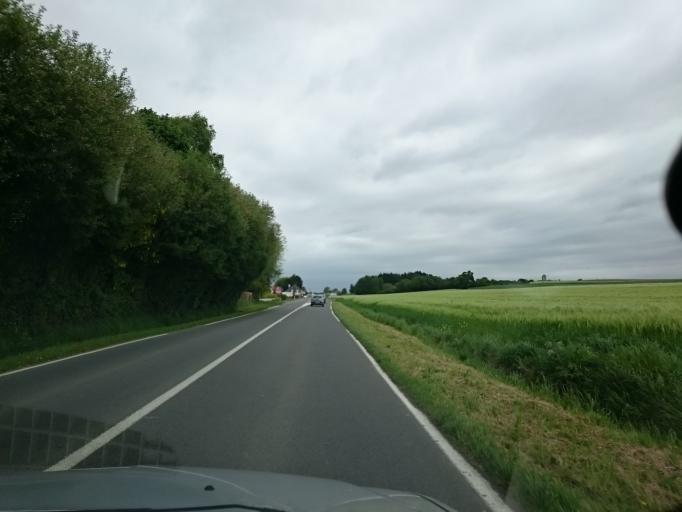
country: FR
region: Lower Normandy
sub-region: Departement de la Manche
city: Pontorson
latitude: 48.5785
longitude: -1.5123
